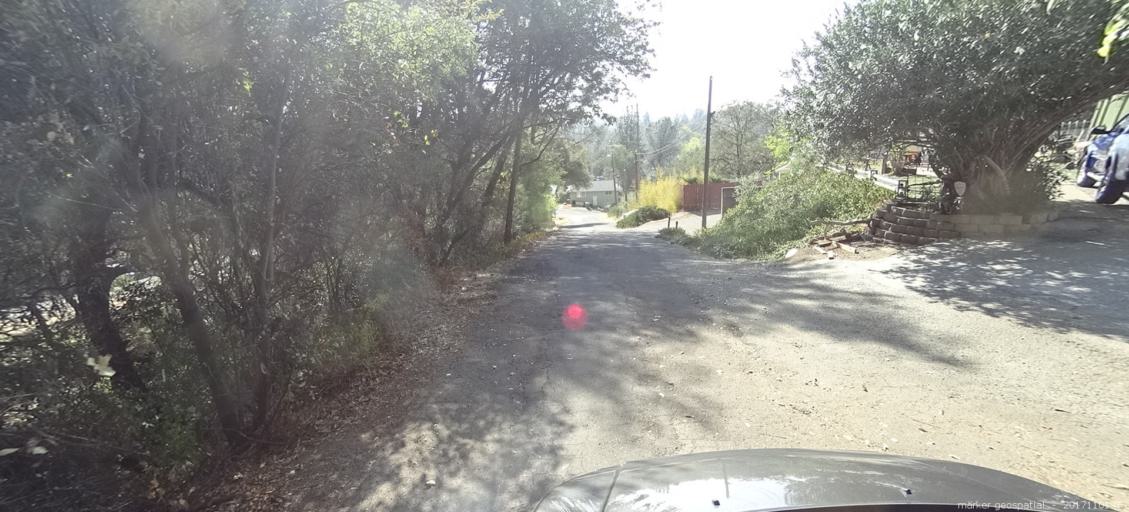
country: US
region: California
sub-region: Shasta County
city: Central Valley (historical)
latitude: 40.6859
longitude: -122.3761
